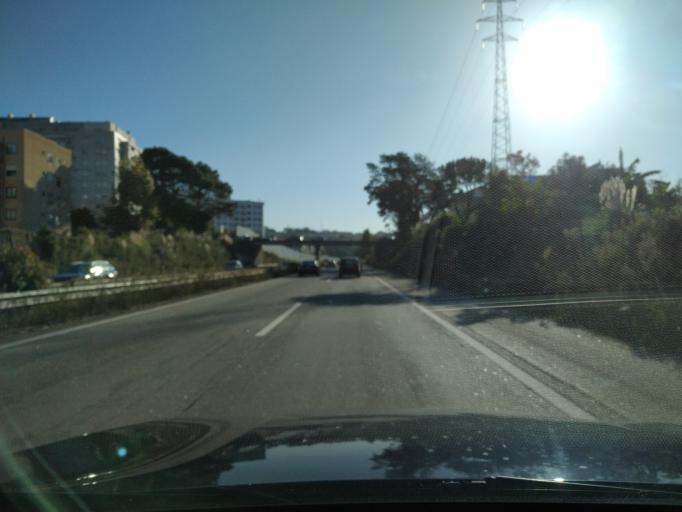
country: PT
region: Porto
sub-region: Vila Nova de Gaia
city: Vila Nova de Gaia
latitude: 41.1130
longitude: -8.6168
